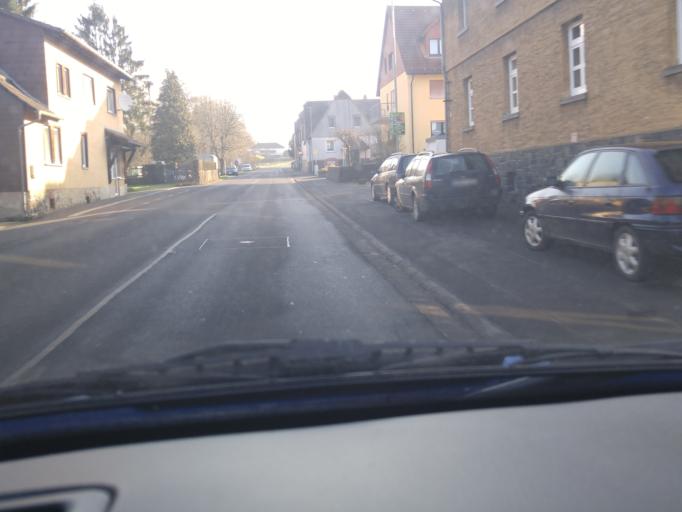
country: DE
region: Hesse
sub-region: Regierungsbezirk Giessen
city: Schotten
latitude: 50.5064
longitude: 9.1316
